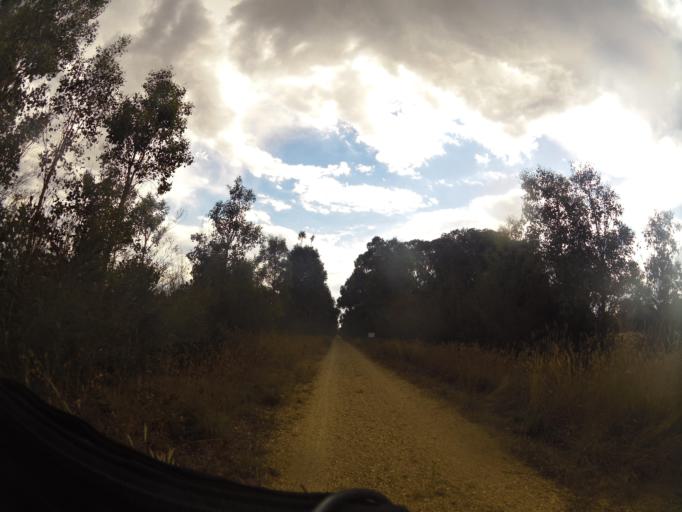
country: AU
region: Victoria
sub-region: Wellington
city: Heyfield
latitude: -38.0336
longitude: 146.6578
